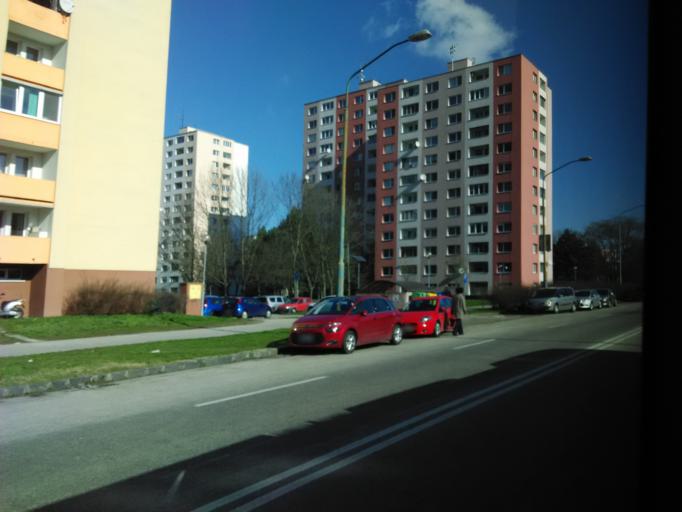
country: SK
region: Bratislavsky
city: Bratislava
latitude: 48.1235
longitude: 17.1301
